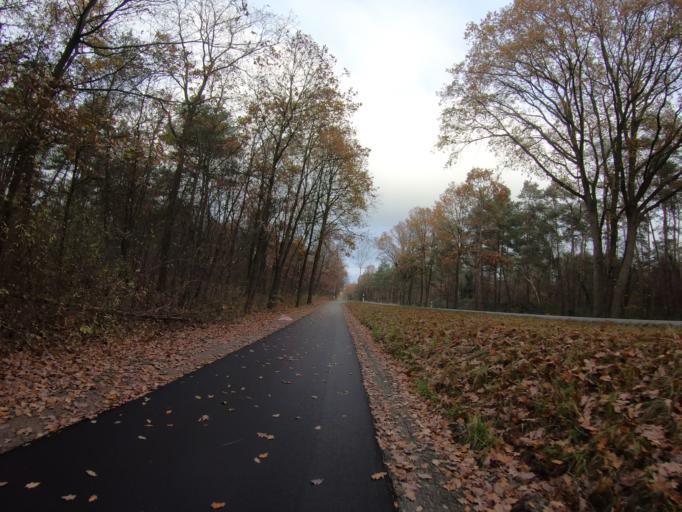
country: DE
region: Lower Saxony
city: Wesendorf
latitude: 52.5772
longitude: 10.5253
